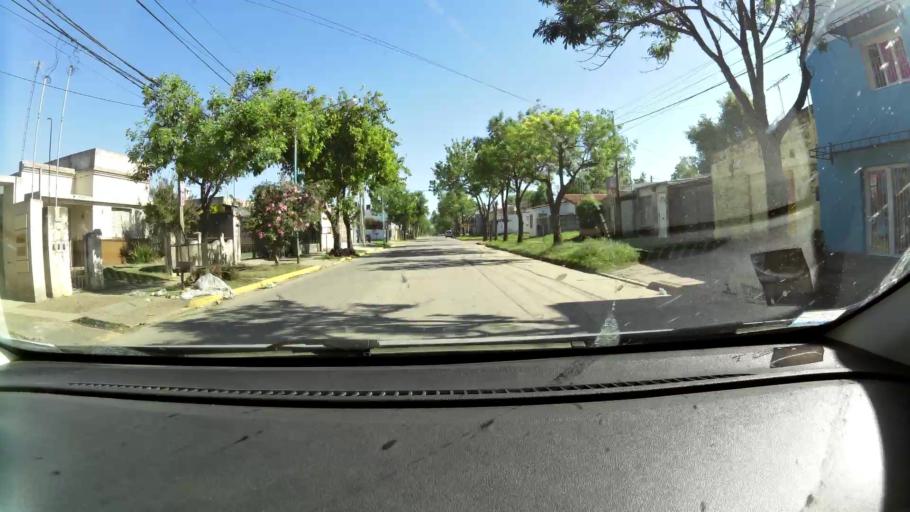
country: AR
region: Santa Fe
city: Rafaela
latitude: -31.2406
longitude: -61.4748
